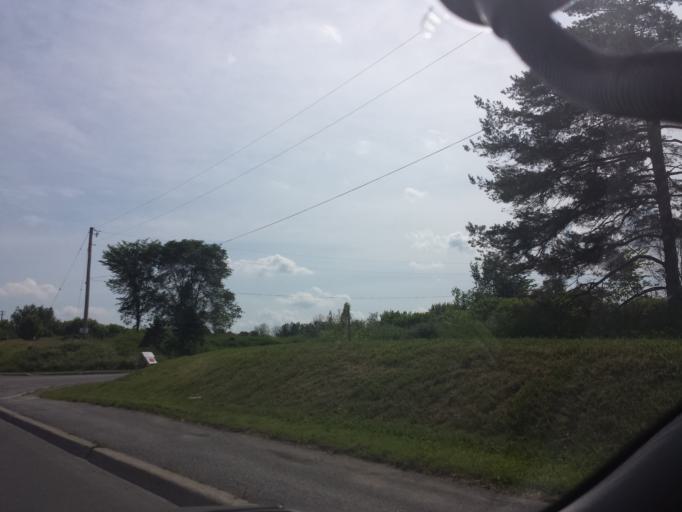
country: CA
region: Ontario
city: Bells Corners
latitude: 45.3330
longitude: -75.8141
